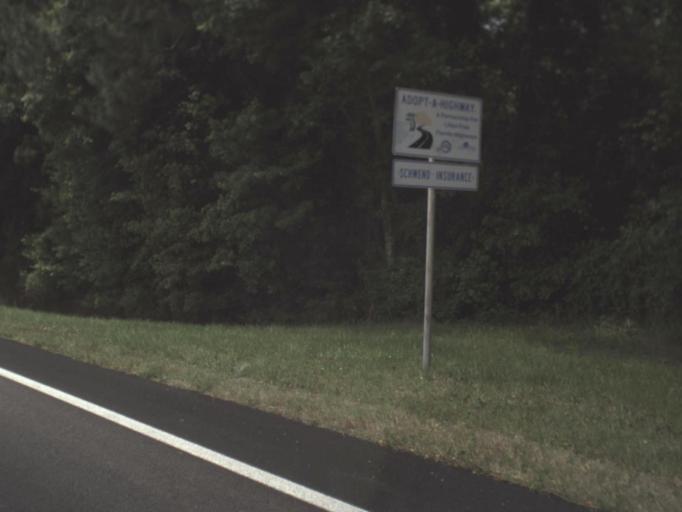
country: US
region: Florida
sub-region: Nassau County
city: Nassau Village-Ratliff
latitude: 30.4409
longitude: -81.7652
